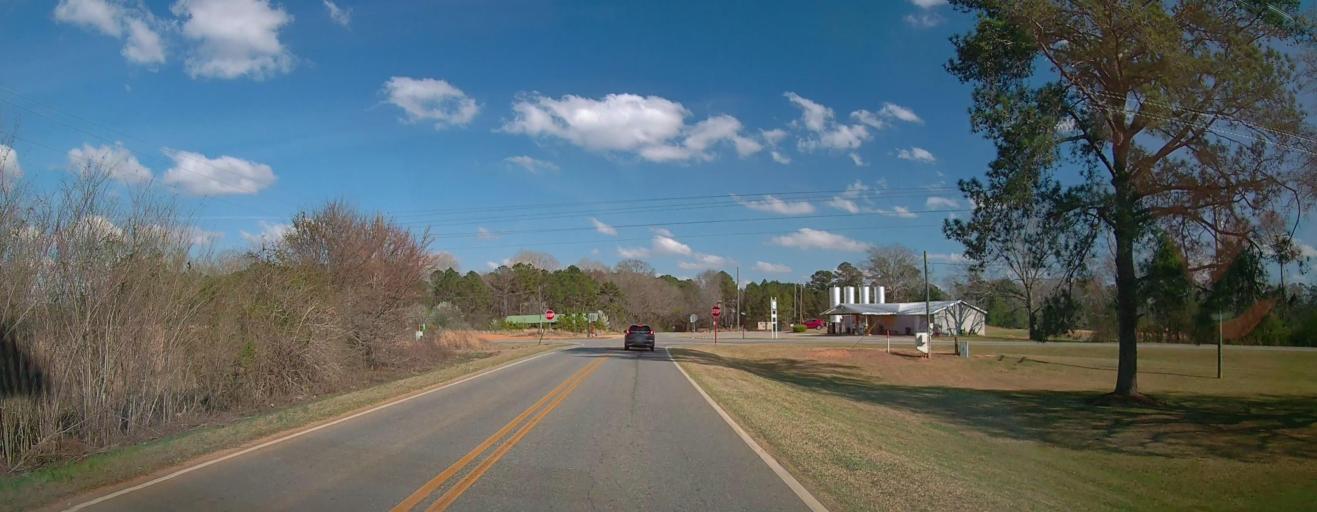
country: US
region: Georgia
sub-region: Laurens County
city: Dublin
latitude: 32.5687
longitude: -83.0339
